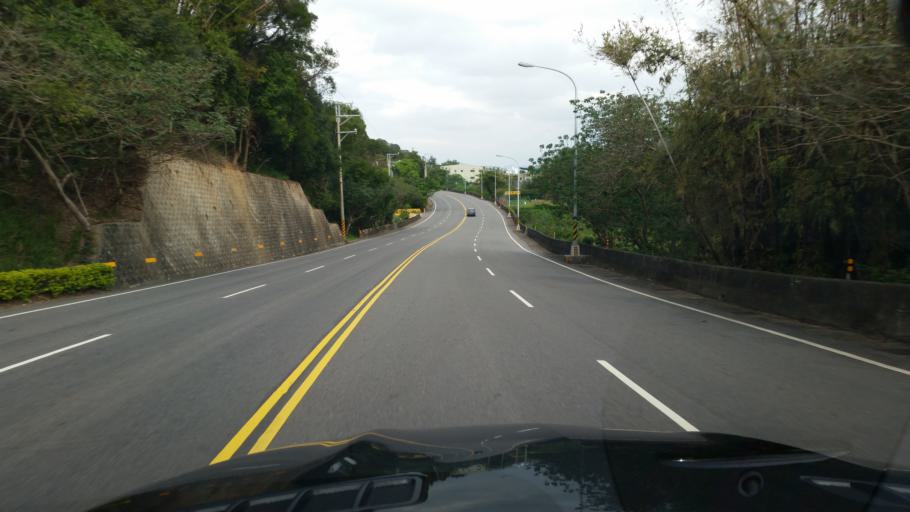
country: TW
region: Taiwan
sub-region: Miaoli
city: Miaoli
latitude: 24.6492
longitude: 120.8624
